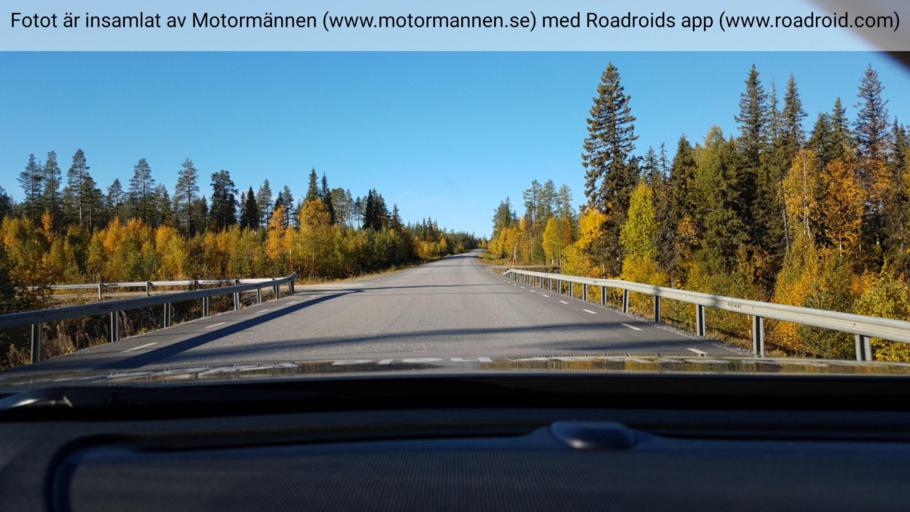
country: SE
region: Vaesterbotten
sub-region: Skelleftea Kommun
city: Storvik
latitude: 65.3342
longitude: 20.8560
